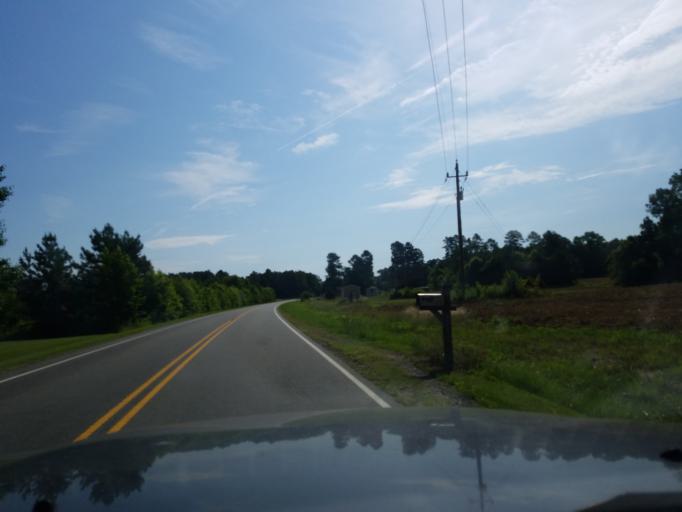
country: US
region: North Carolina
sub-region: Granville County
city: Oxford
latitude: 36.2479
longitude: -78.6882
